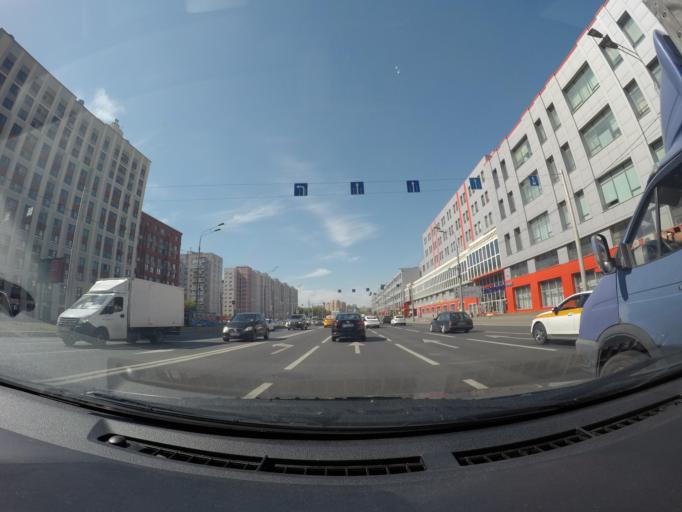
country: RU
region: Moscow
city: Lefortovo
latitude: 55.7329
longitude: 37.7137
